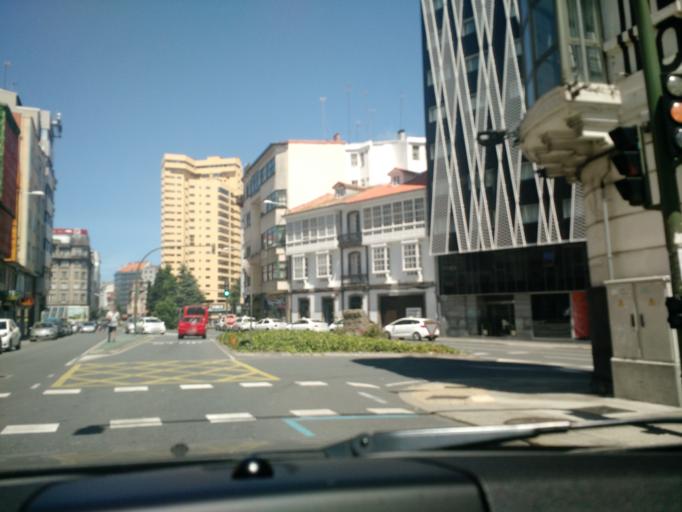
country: ES
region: Galicia
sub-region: Provincia da Coruna
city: A Coruna
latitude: 43.3558
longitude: -8.4047
